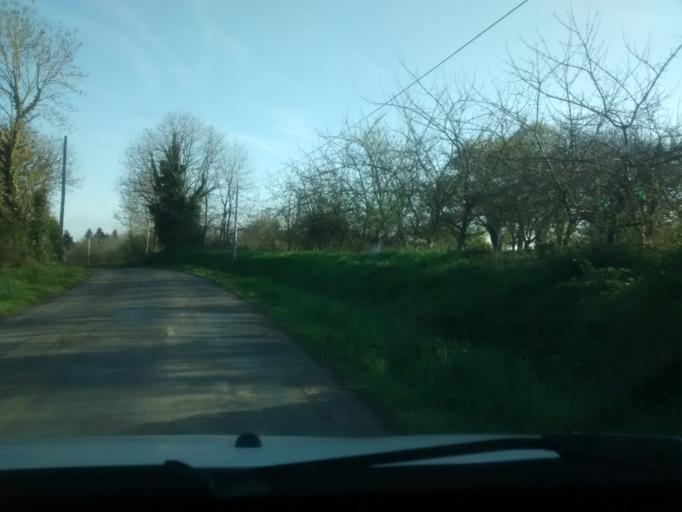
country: FR
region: Brittany
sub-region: Departement d'Ille-et-Vilaine
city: Saint-Broladre
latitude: 48.5753
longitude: -1.6437
